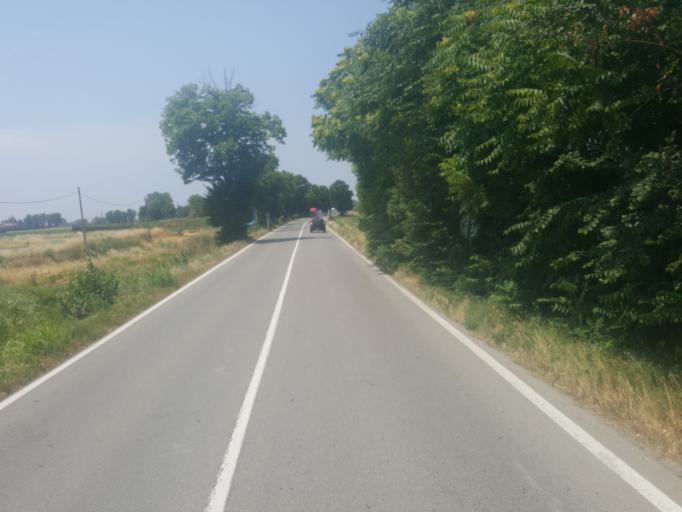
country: IT
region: Emilia-Romagna
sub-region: Provincia di Modena
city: Cavazzona
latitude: 44.5746
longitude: 11.1116
